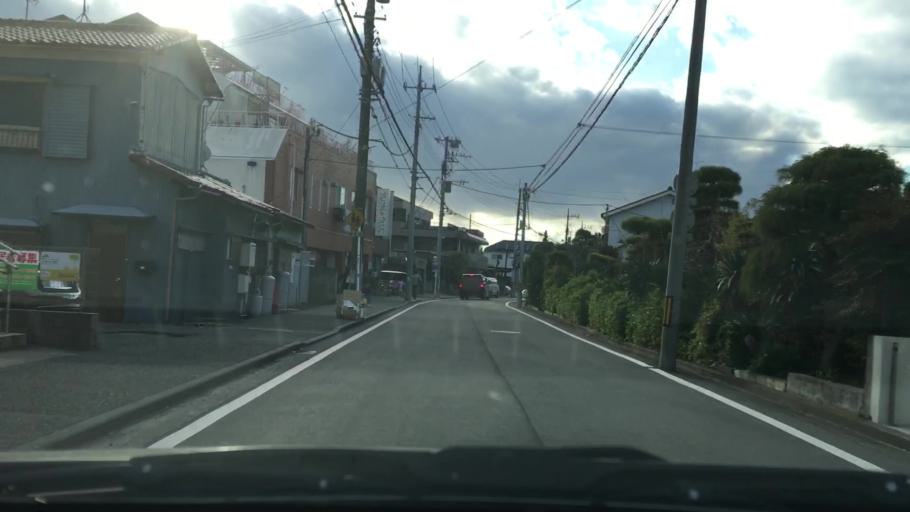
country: JP
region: Kanagawa
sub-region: Kawasaki-shi
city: Kawasaki
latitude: 35.5254
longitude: 139.6417
